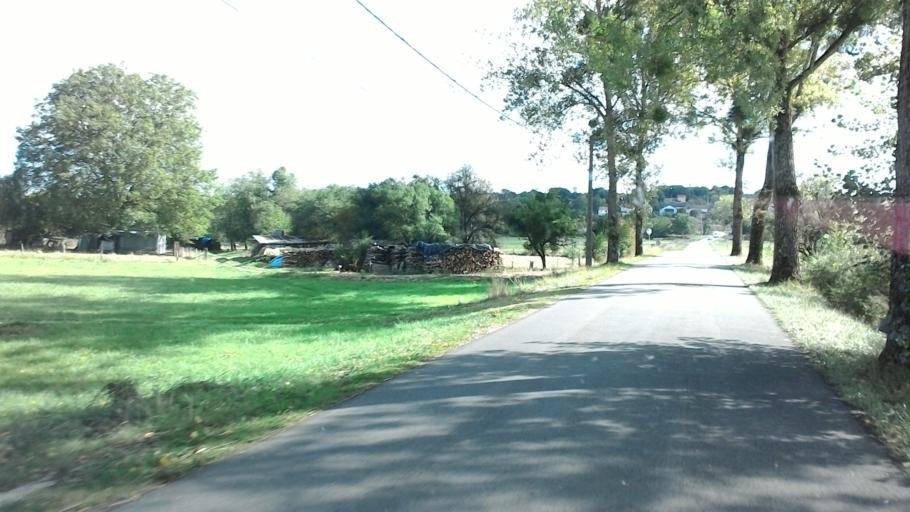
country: FR
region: Lorraine
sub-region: Departement des Vosges
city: Neufchateau
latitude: 48.3691
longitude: 5.6824
